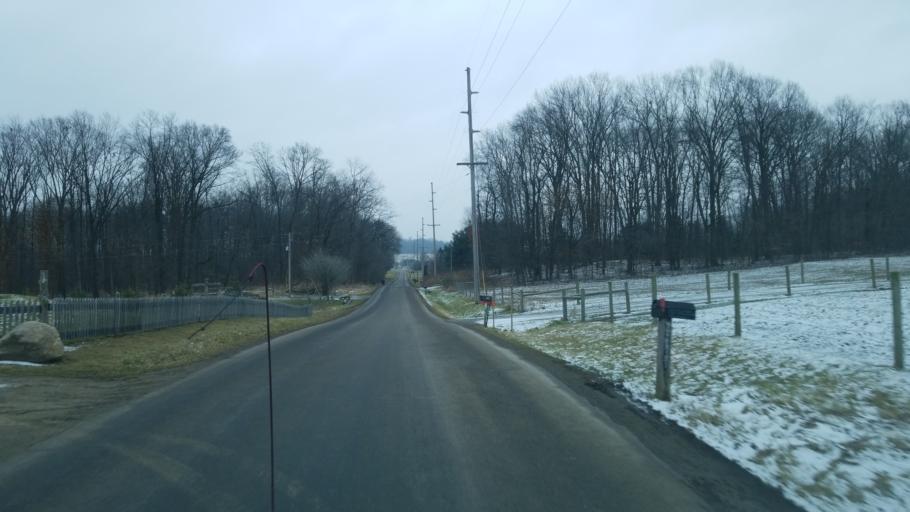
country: US
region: Ohio
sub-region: Wayne County
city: Apple Creek
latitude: 40.7111
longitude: -81.8878
